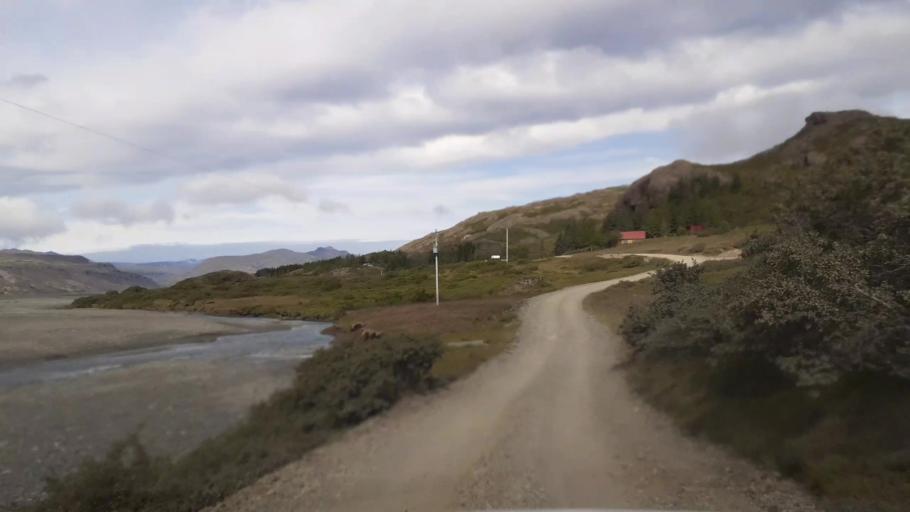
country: IS
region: East
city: Hoefn
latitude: 64.4338
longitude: -14.8949
